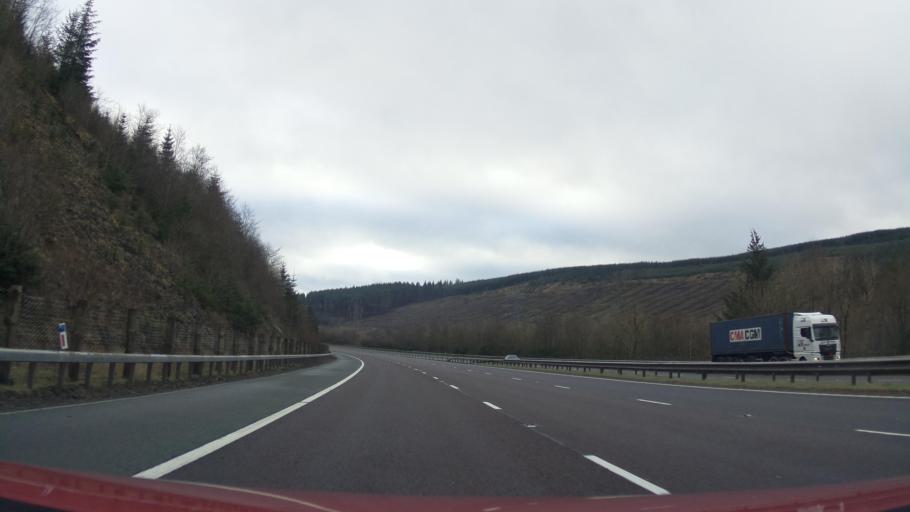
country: GB
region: Scotland
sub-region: Dumfries and Galloway
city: Moffat
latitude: 55.3645
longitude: -3.5151
